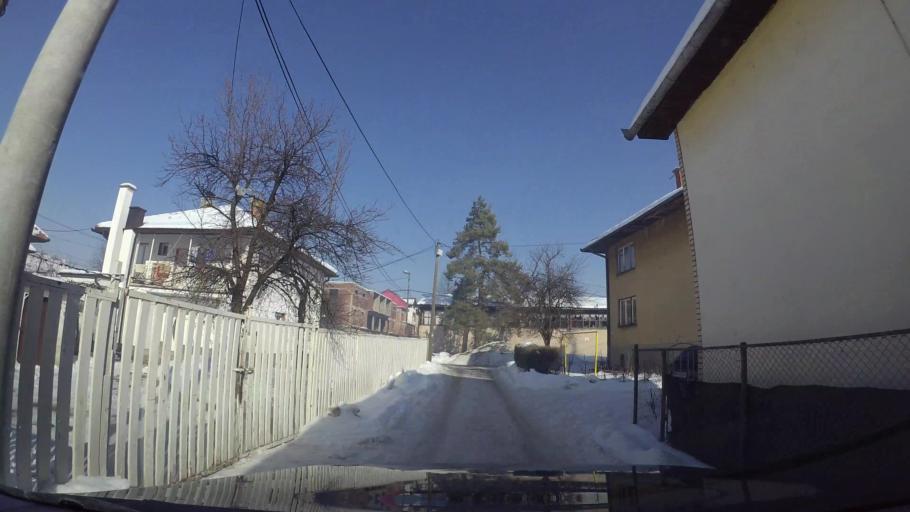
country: BA
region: Federation of Bosnia and Herzegovina
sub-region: Kanton Sarajevo
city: Sarajevo
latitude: 43.7960
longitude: 18.3132
